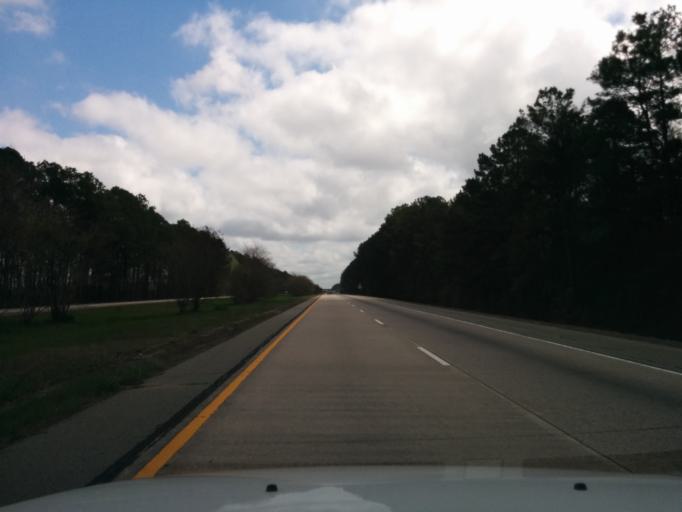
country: US
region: Georgia
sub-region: Bryan County
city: Pembroke
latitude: 32.1885
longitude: -81.4699
